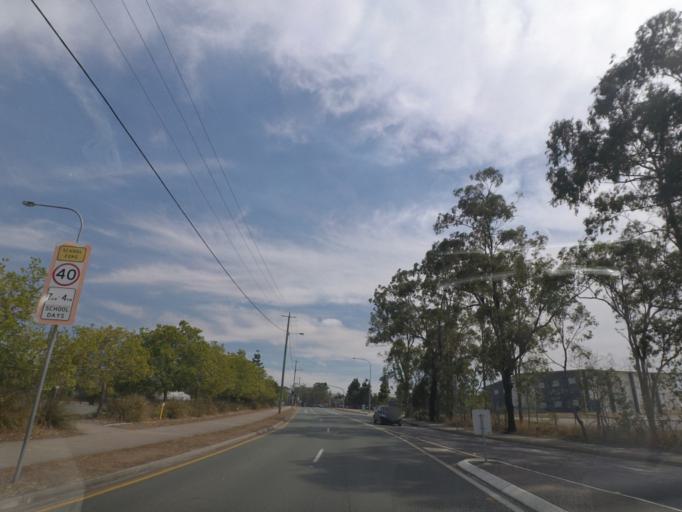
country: AU
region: Queensland
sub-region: Brisbane
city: Sunnybank Hills
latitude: -27.6377
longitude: 153.0573
